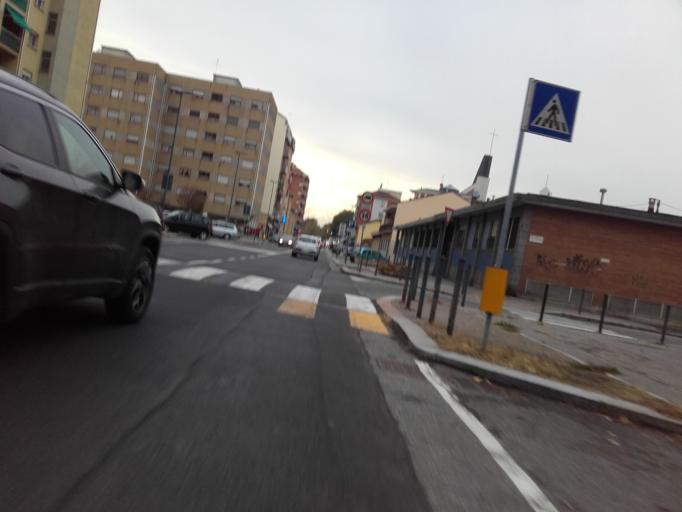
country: IT
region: Piedmont
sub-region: Provincia di Torino
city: Turin
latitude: 45.1146
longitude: 7.7060
